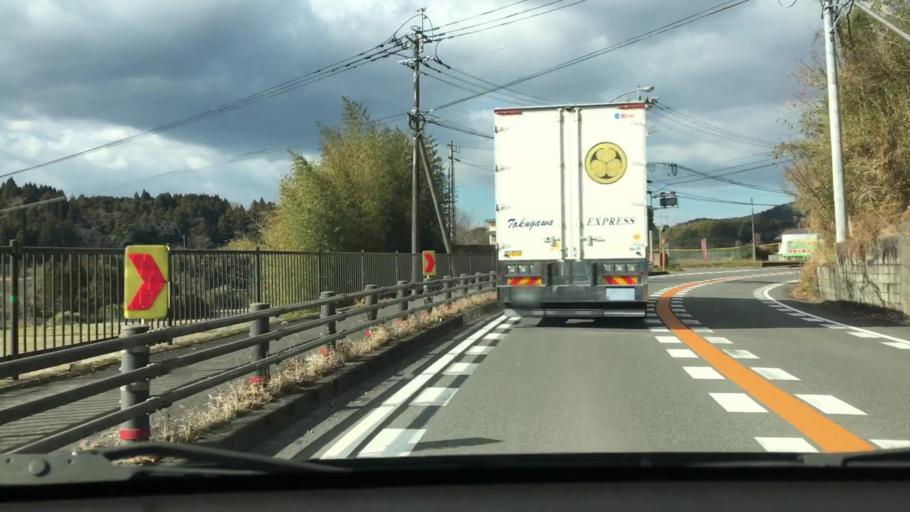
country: JP
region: Oita
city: Usuki
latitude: 33.0499
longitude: 131.6891
